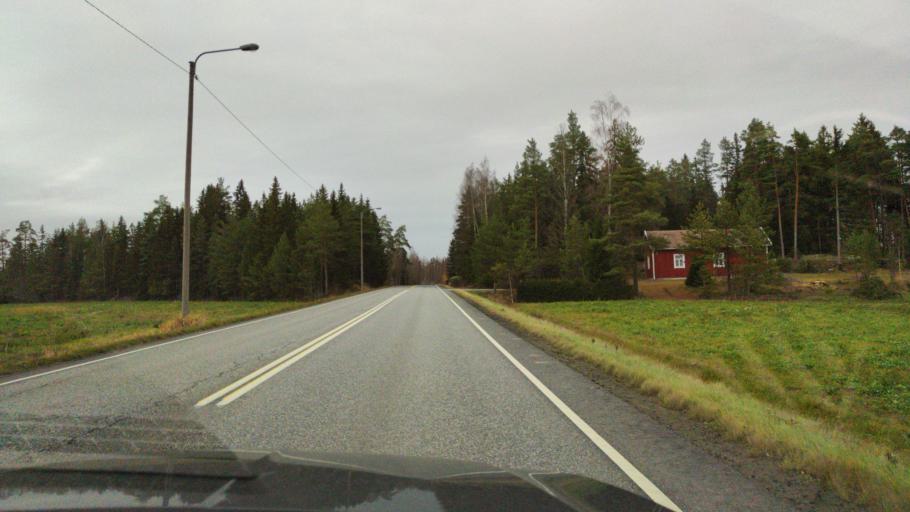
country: FI
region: Varsinais-Suomi
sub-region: Turku
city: Vahto
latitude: 60.6396
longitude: 22.4197
